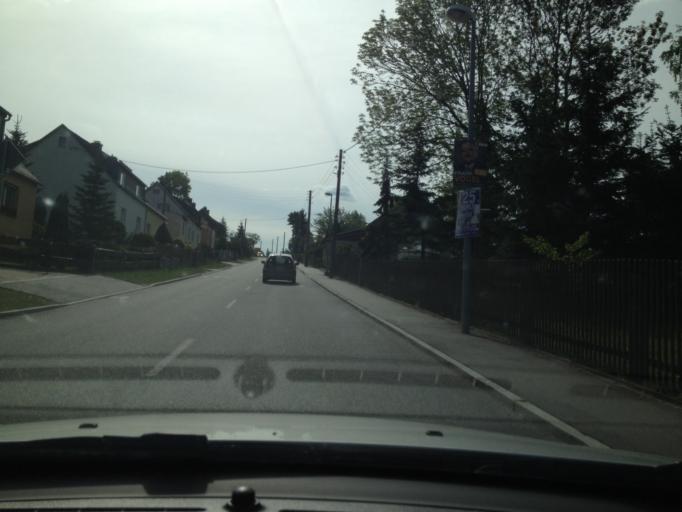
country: DE
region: Saxony
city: Annaberg-Buchholz
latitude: 50.5500
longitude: 13.0117
